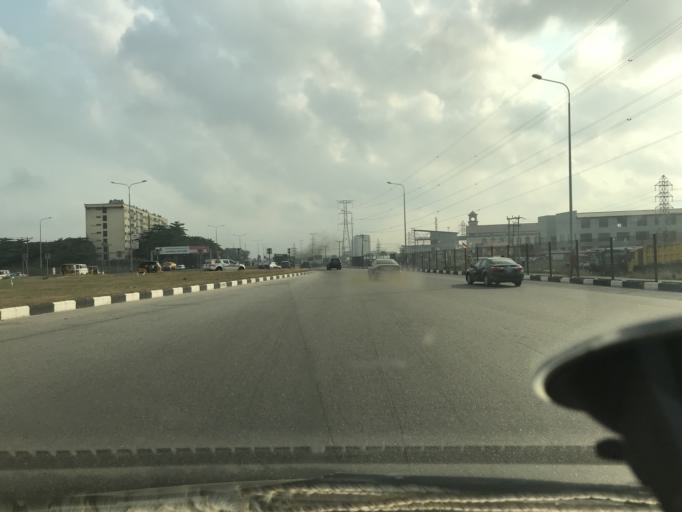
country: NG
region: Lagos
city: Ikoyi
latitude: 6.4453
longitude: 3.5408
